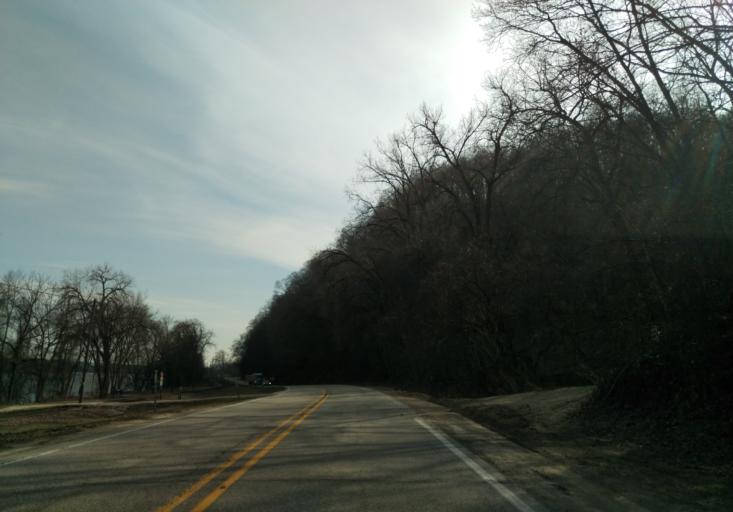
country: US
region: Wisconsin
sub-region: Crawford County
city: Prairie du Chien
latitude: 43.0826
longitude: -91.1807
